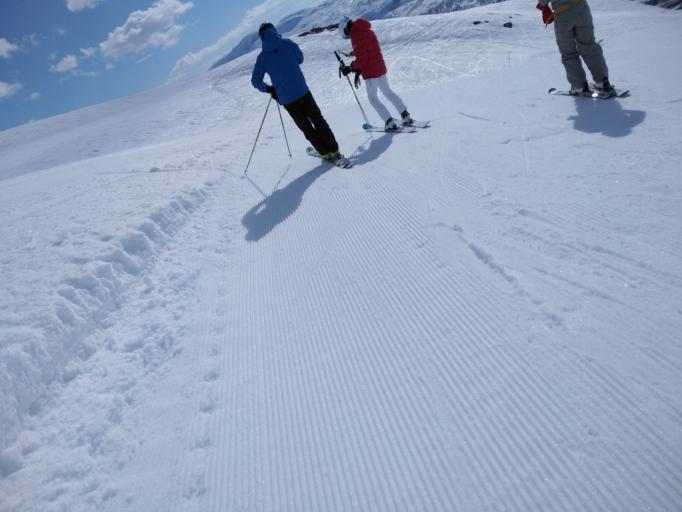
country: NO
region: Sogn og Fjordane
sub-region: Vik
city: Vik
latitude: 60.8774
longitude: 6.4671
